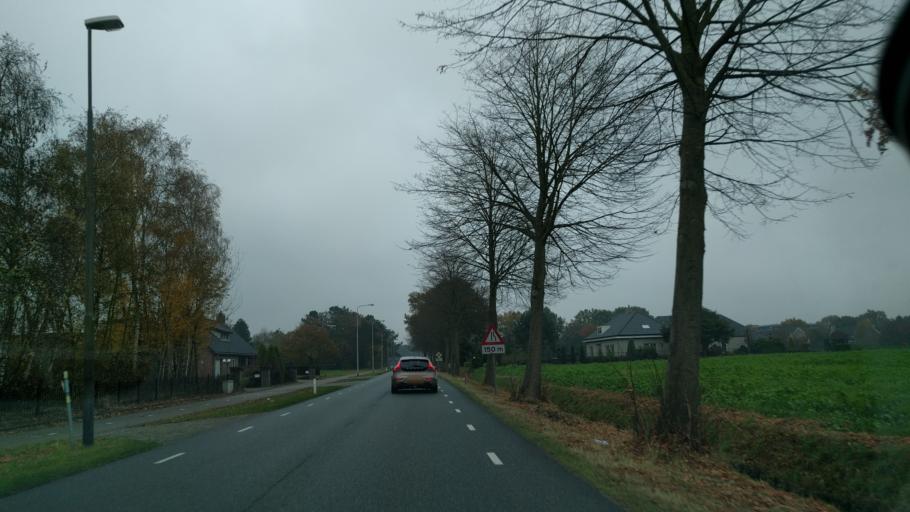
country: NL
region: North Brabant
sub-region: Gemeente Rucphen
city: Rucphen
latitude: 51.5344
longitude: 4.5445
